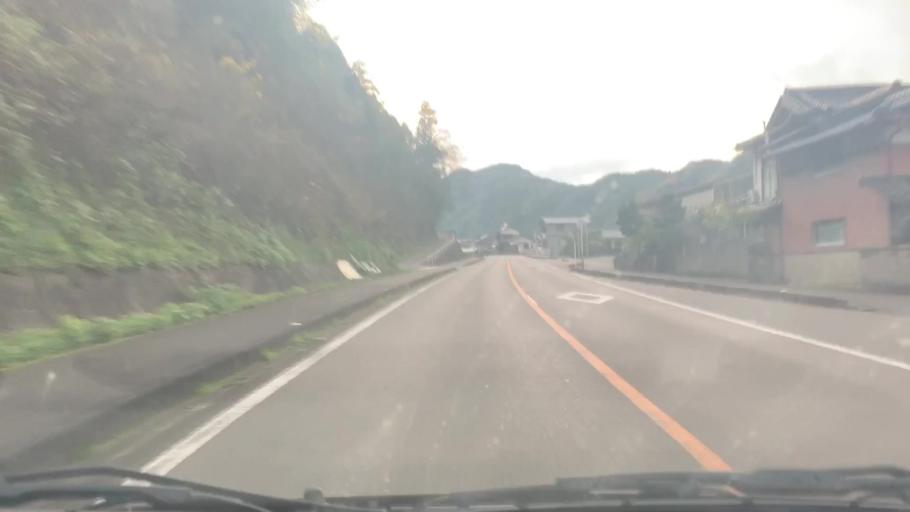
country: JP
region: Saga Prefecture
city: Kashima
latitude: 33.0858
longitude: 130.0777
